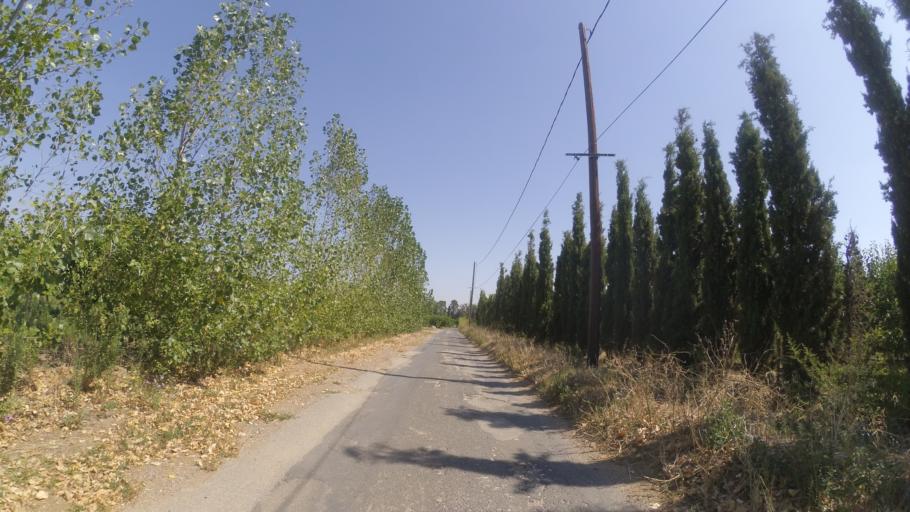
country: FR
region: Languedoc-Roussillon
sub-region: Departement des Pyrenees-Orientales
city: Corneilla-la-Riviere
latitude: 42.6600
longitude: 2.7205
